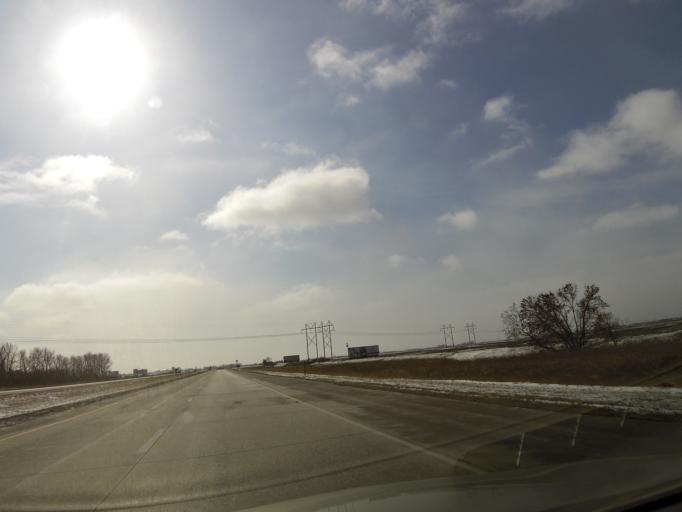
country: US
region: North Dakota
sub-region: Grand Forks County
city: Grand Forks
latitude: 47.9730
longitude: -97.0949
